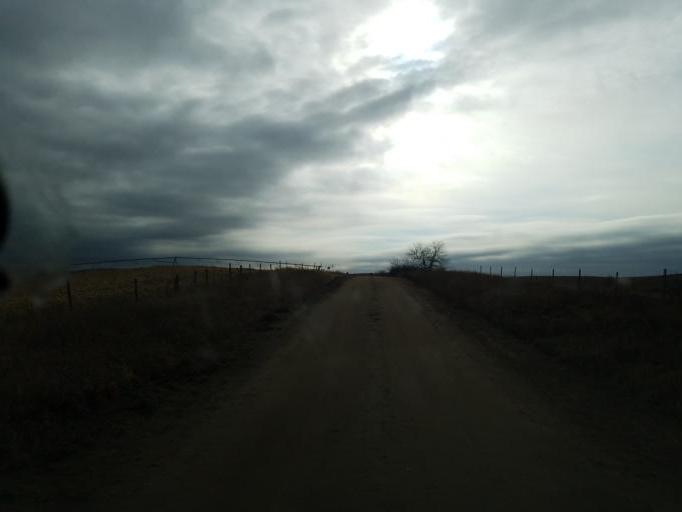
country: US
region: Nebraska
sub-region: Knox County
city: Center
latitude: 42.6057
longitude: -97.8379
